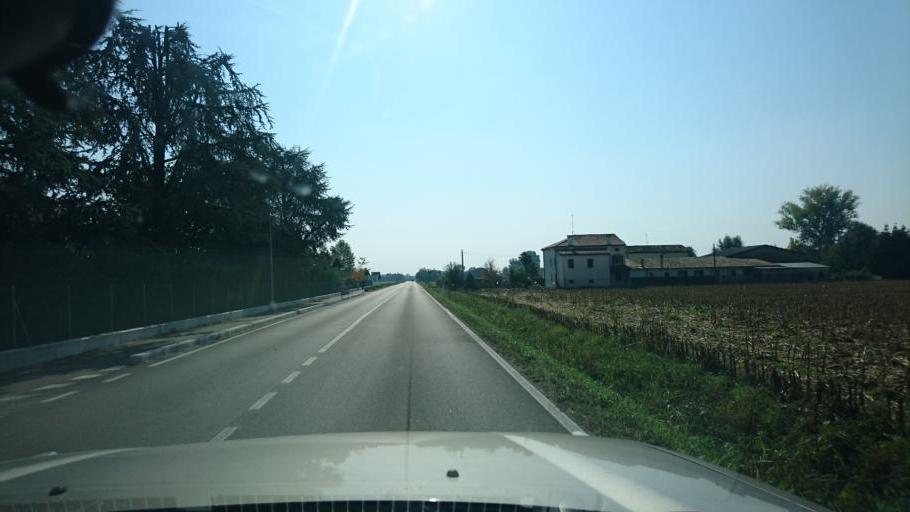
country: IT
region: Veneto
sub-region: Provincia di Padova
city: Gazzo
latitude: 45.5779
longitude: 11.7085
